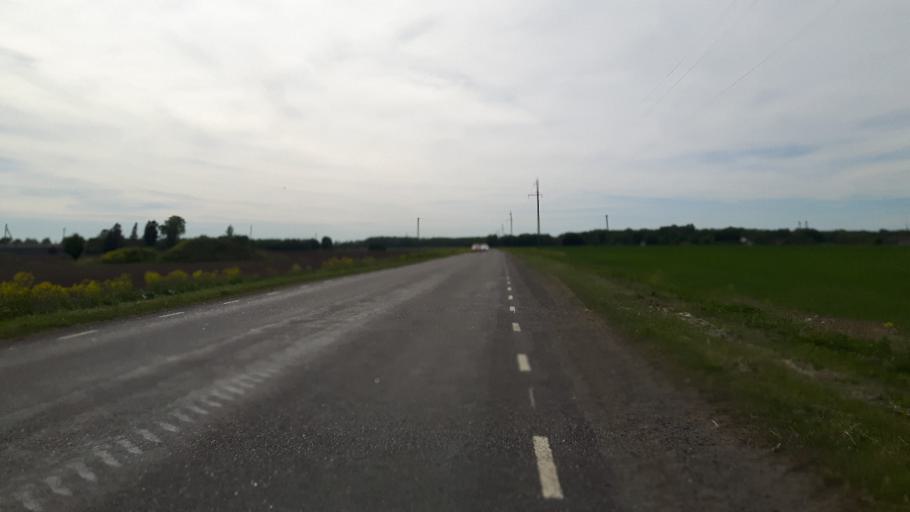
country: EE
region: Harju
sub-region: Maardu linn
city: Maardu
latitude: 59.4255
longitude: 25.0383
